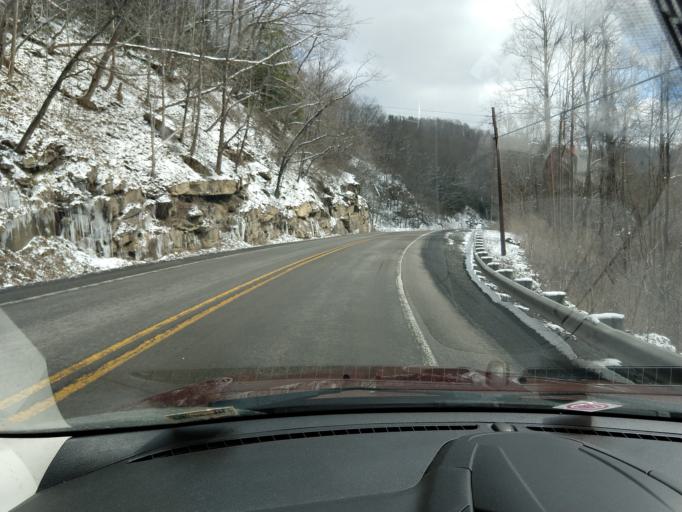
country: US
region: West Virginia
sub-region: Nicholas County
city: Craigsville
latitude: 38.2996
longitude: -80.6457
